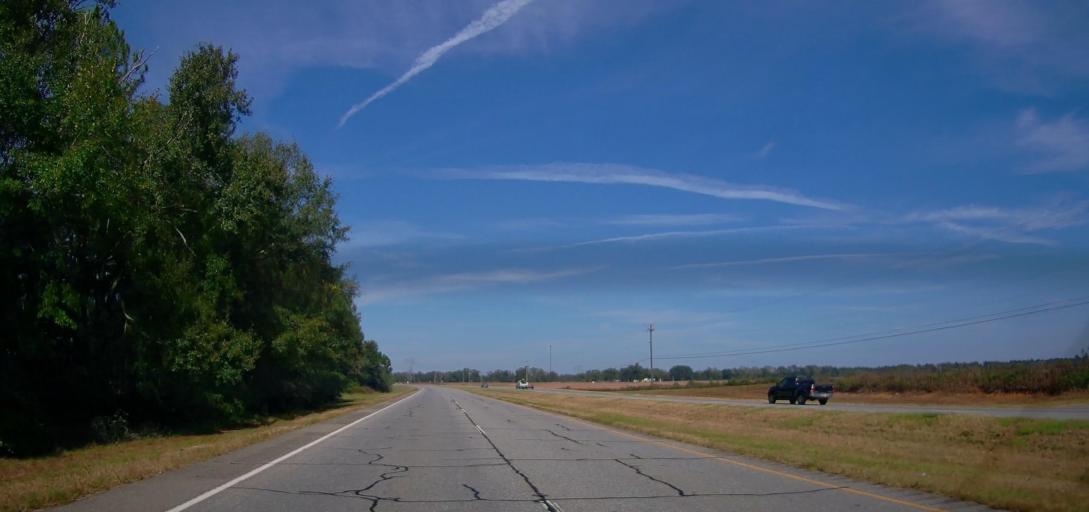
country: US
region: Georgia
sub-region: Dougherty County
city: Putney
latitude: 31.3577
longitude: -84.1578
